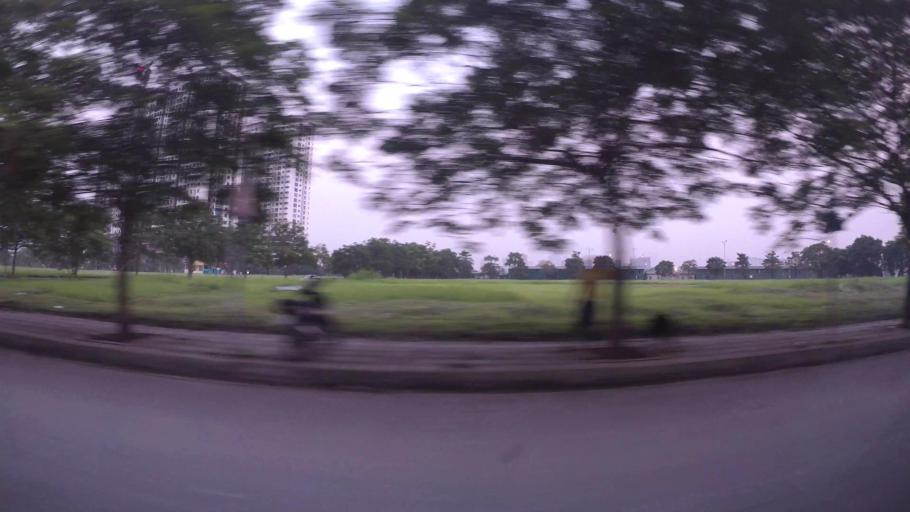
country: VN
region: Ha Noi
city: Tay Ho
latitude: 21.0649
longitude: 105.7922
